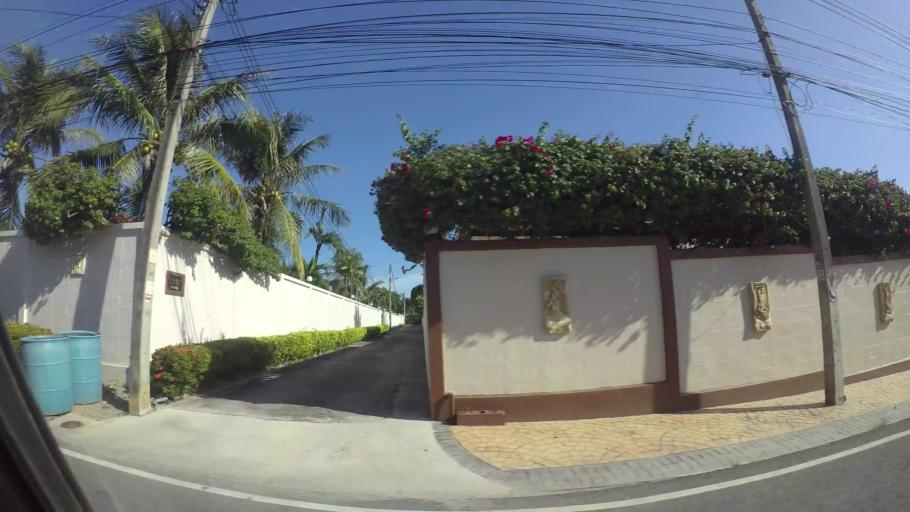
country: TH
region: Chon Buri
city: Phatthaya
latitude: 12.9026
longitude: 100.8985
